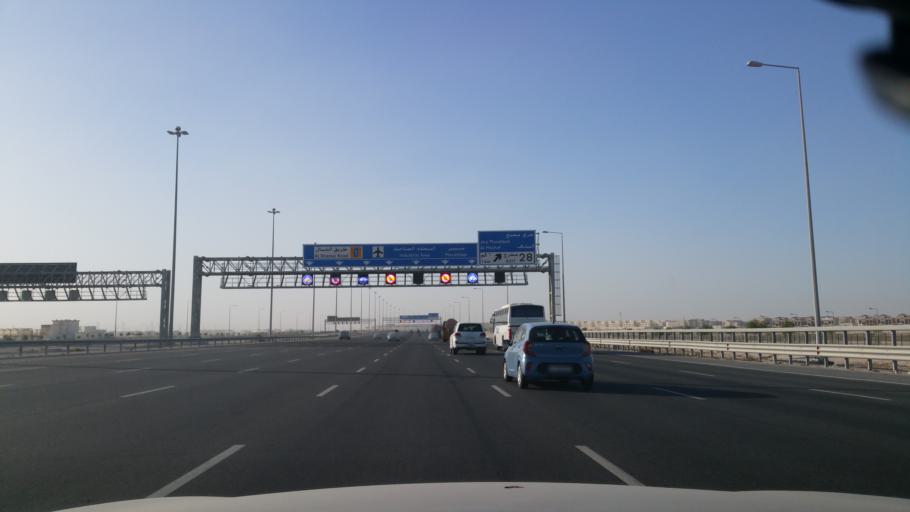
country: QA
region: Al Wakrah
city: Al Wukayr
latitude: 25.1698
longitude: 51.5604
